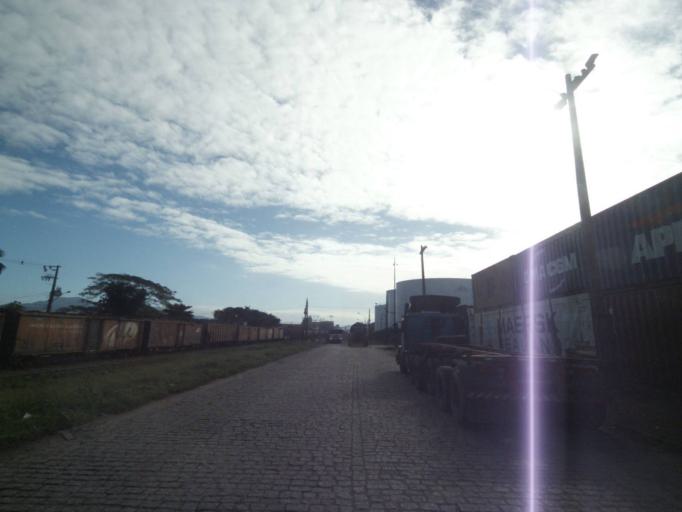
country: BR
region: Parana
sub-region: Paranagua
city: Paranagua
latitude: -25.5196
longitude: -48.5268
